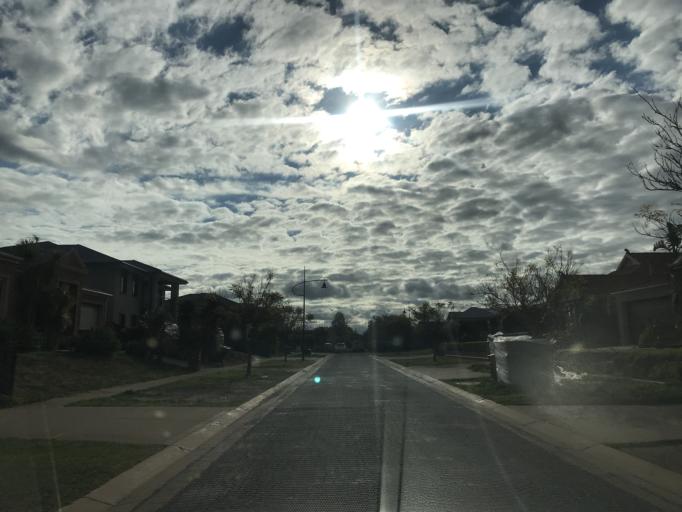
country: AU
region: Victoria
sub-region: Wyndham
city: Point Cook
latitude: -37.8935
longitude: 144.7367
